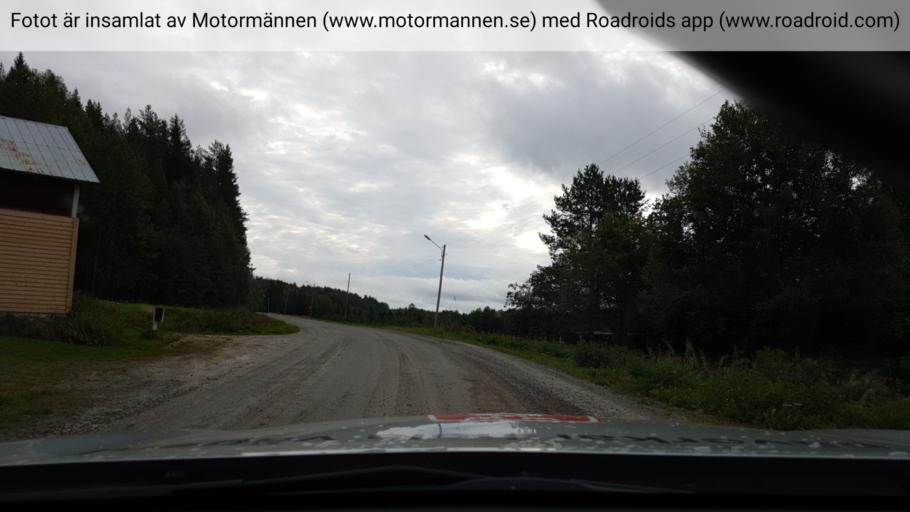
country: SE
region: Vaesterbotten
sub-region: Vannas Kommun
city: Vannasby
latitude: 64.0987
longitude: 20.0043
